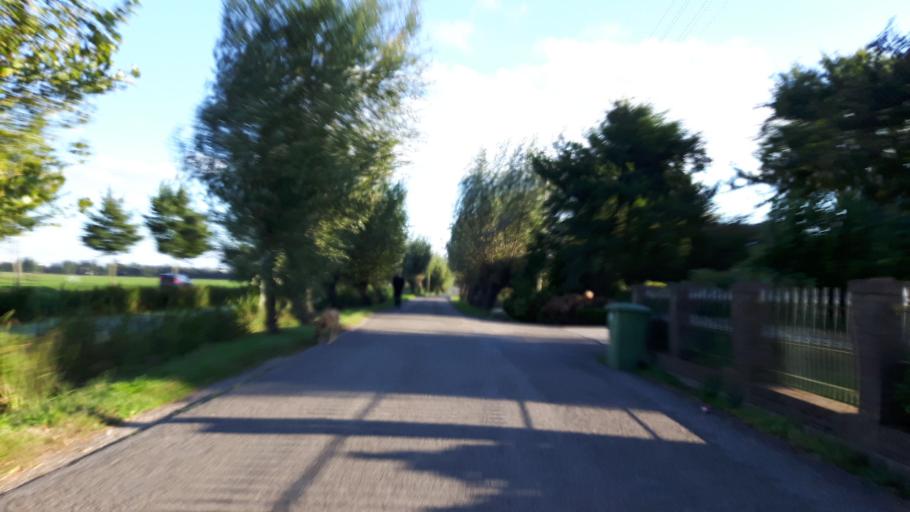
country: NL
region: Utrecht
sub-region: Gemeente Oudewater
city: Oudewater
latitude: 52.0416
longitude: 4.8555
